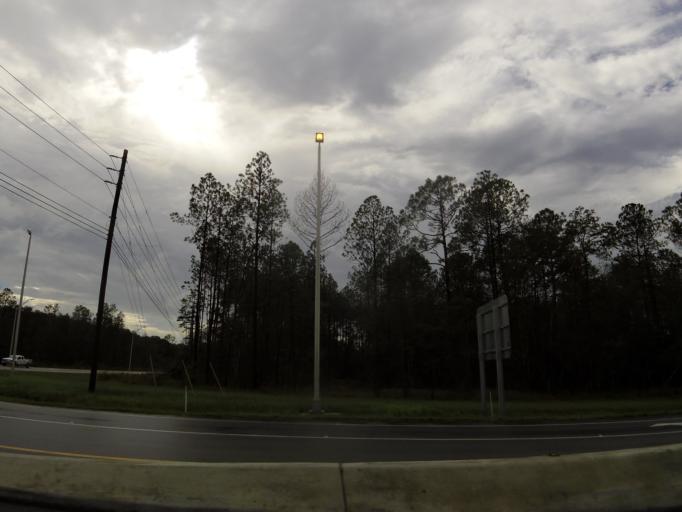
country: US
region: Florida
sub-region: Duval County
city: Baldwin
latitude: 30.3111
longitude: -81.8825
